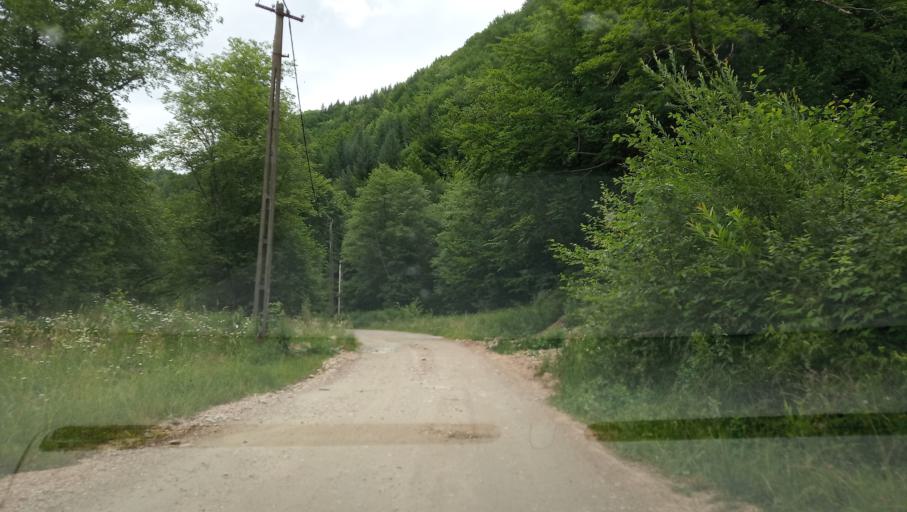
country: RO
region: Hunedoara
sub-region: Oras Petrila
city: Petrila
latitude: 45.4857
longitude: 23.4180
